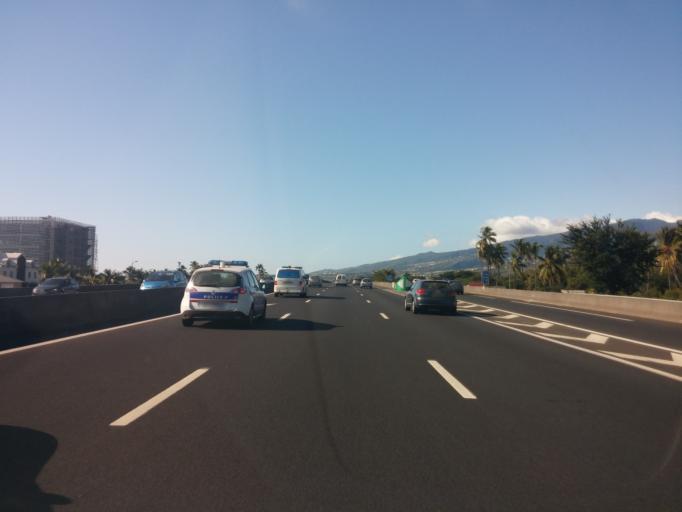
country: RE
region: Reunion
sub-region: Reunion
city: Saint-Paul
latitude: -21.0117
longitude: 55.2748
